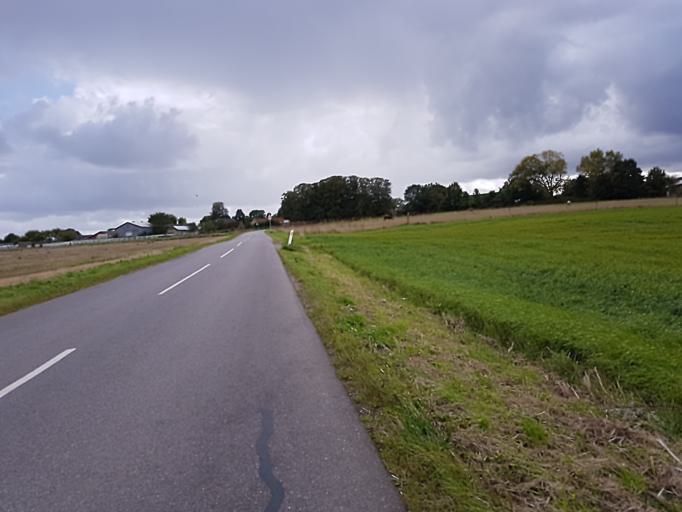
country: DK
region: Zealand
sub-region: Roskilde Kommune
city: Gundsomagle
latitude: 55.7177
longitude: 12.1367
